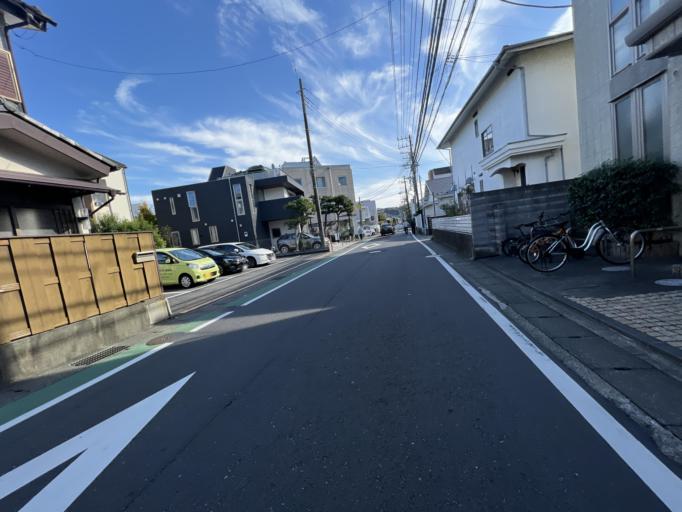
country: JP
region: Kanagawa
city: Kamakura
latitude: 35.3101
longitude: 139.5480
